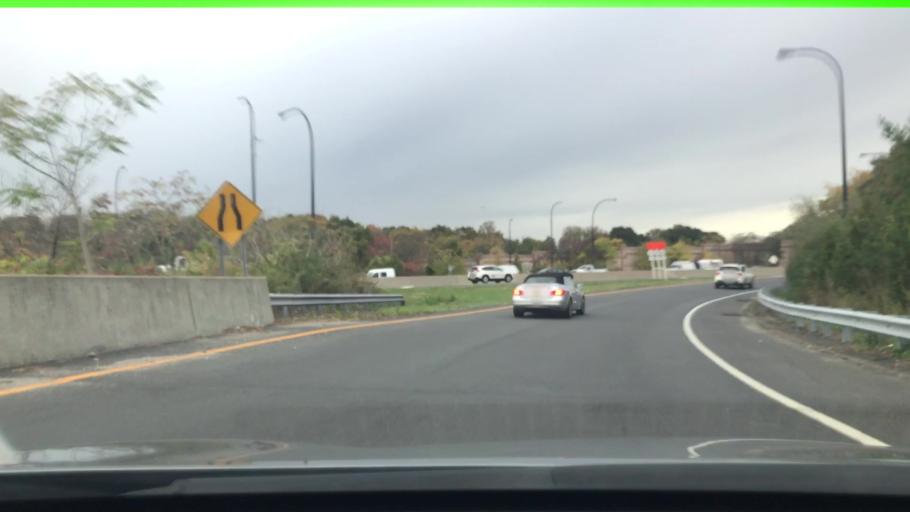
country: US
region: New York
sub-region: Nassau County
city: Syosset
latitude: 40.8001
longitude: -73.4911
